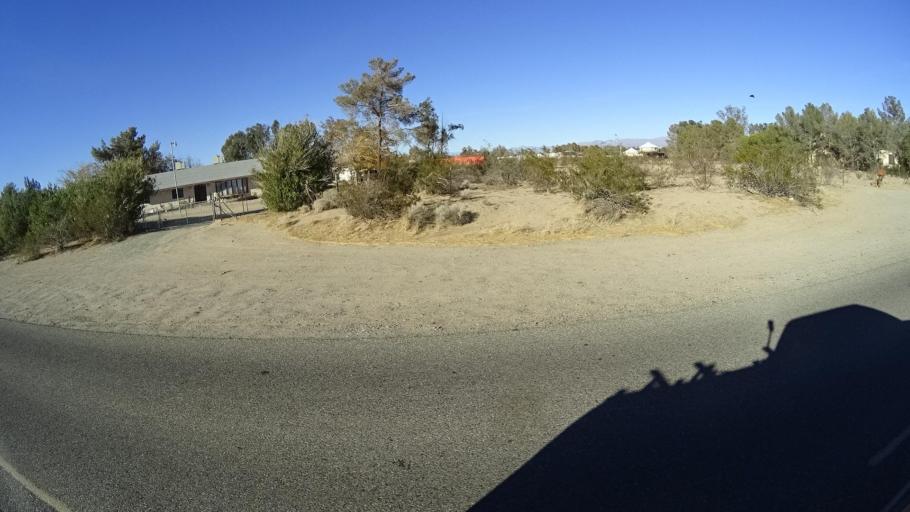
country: US
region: California
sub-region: Kern County
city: Ridgecrest
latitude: 35.6371
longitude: -117.7017
